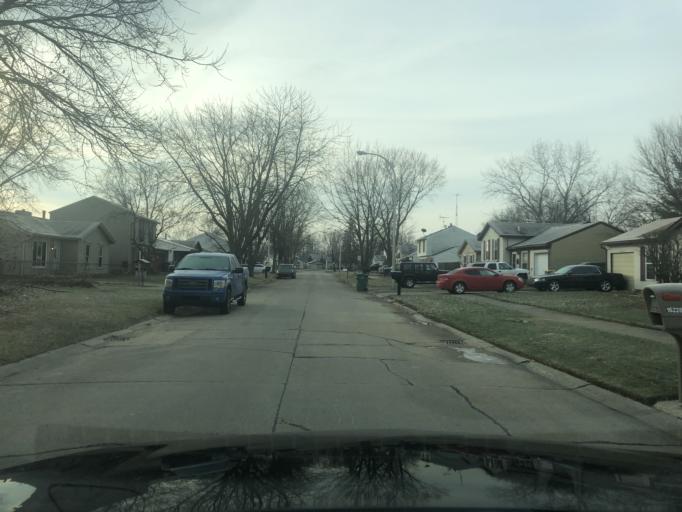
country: US
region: Michigan
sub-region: Wayne County
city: Taylor
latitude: 42.1867
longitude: -83.3213
